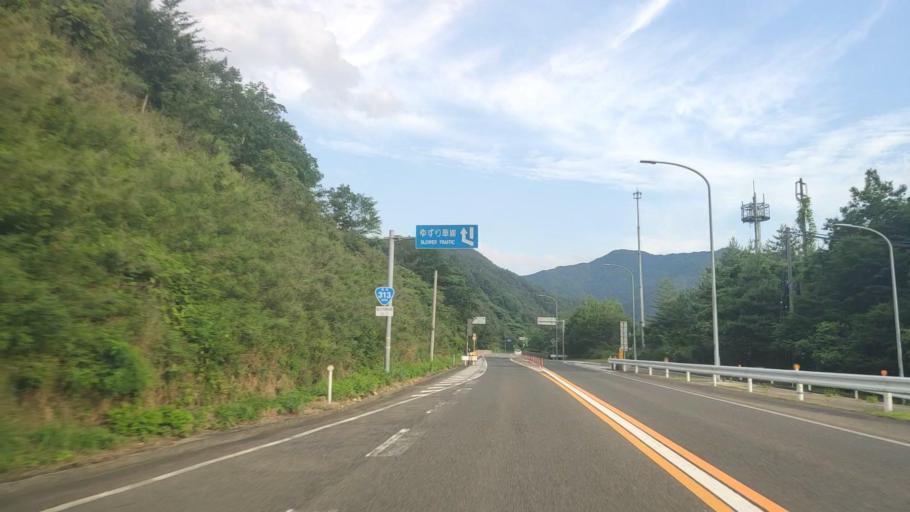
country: JP
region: Tottori
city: Kurayoshi
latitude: 35.3282
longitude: 133.7553
